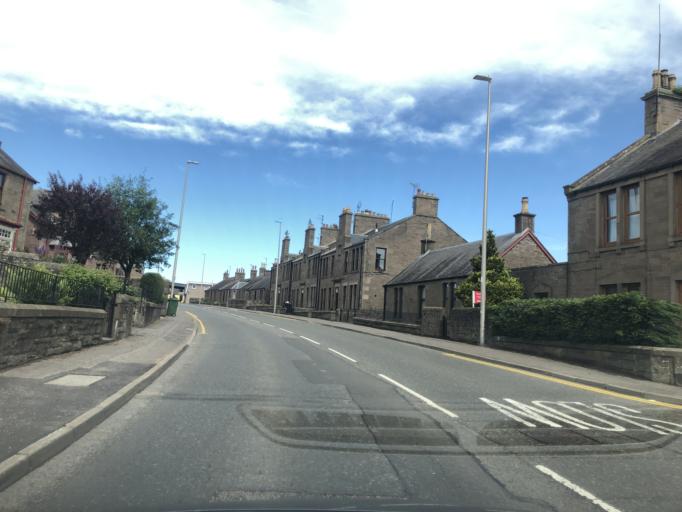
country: GB
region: Scotland
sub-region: Angus
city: Forfar
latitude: 56.6505
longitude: -2.8893
